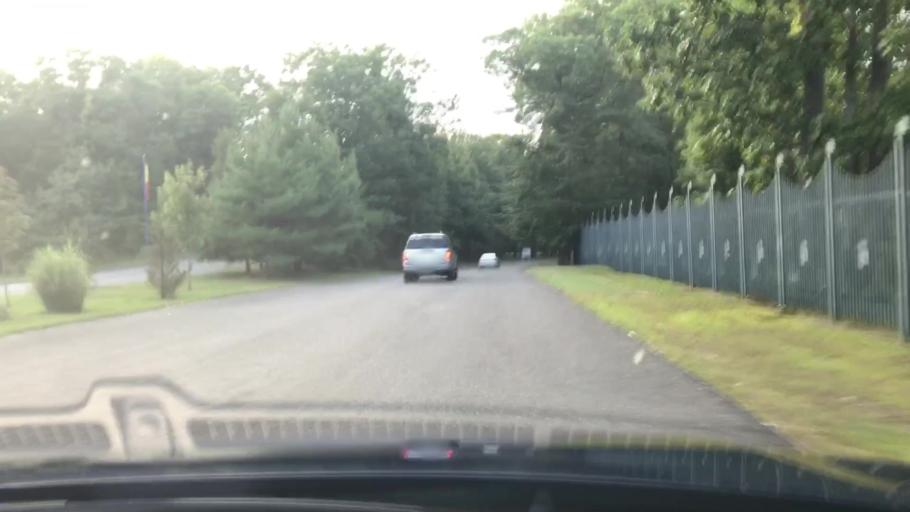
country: US
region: New Jersey
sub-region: Monmouth County
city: Shrewsbury
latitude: 40.1464
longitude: -74.4407
